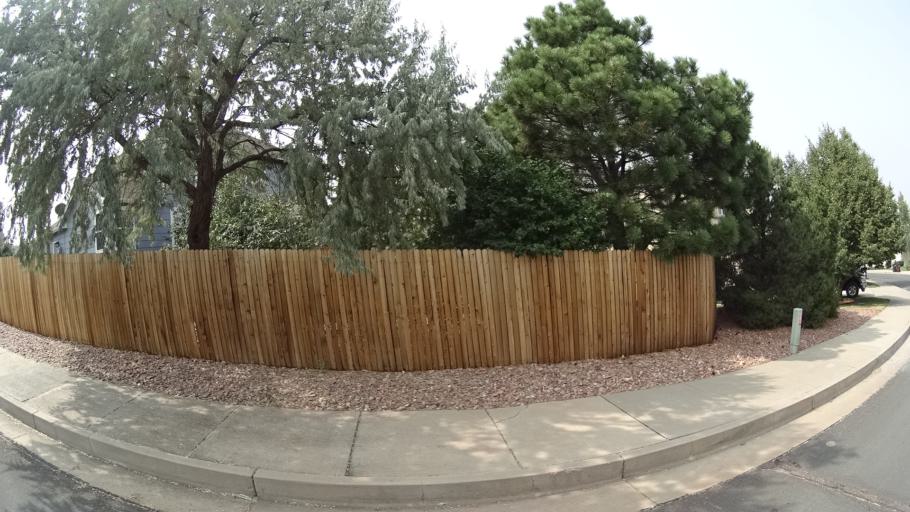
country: US
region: Colorado
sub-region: El Paso County
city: Cimarron Hills
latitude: 38.9163
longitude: -104.7451
